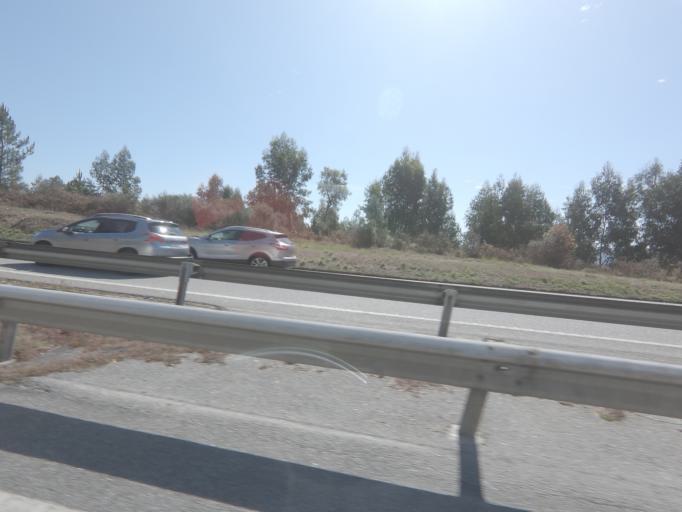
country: PT
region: Porto
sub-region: Paredes
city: Baltar
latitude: 41.1793
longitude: -8.3772
